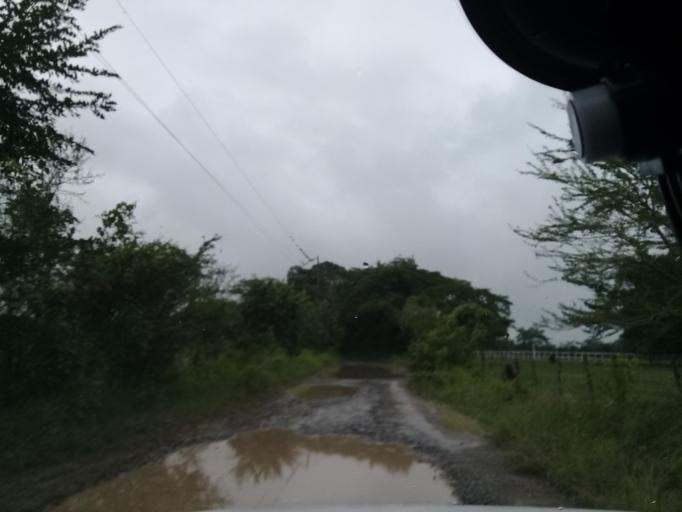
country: MX
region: Veracruz
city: Platon Sanchez
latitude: 21.2485
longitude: -98.3476
